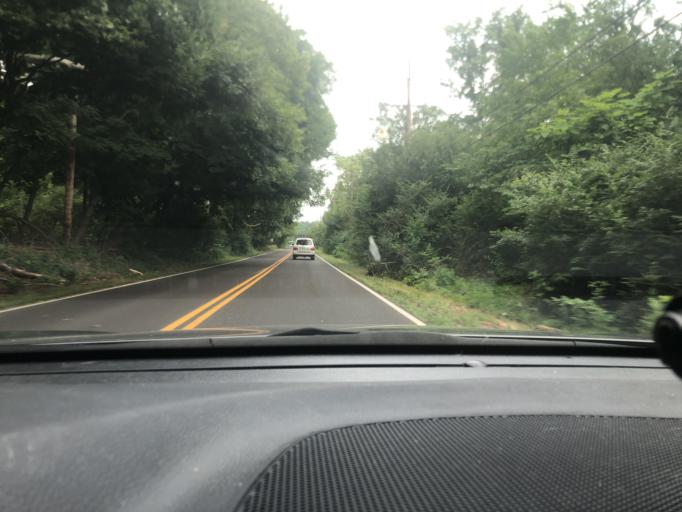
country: US
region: Pennsylvania
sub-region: Montgomery County
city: Spring House
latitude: 40.1892
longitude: -75.2339
